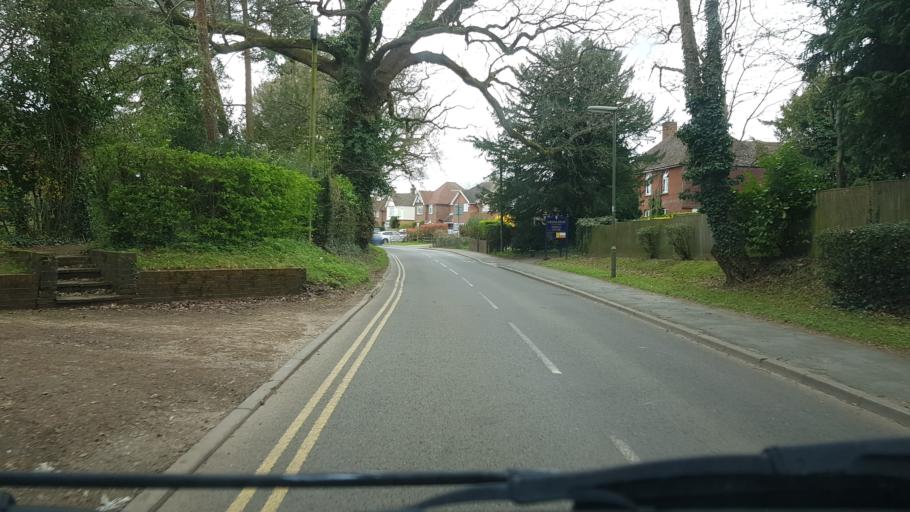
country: GB
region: England
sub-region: Surrey
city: Cranleigh
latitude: 51.1476
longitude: -0.4951
